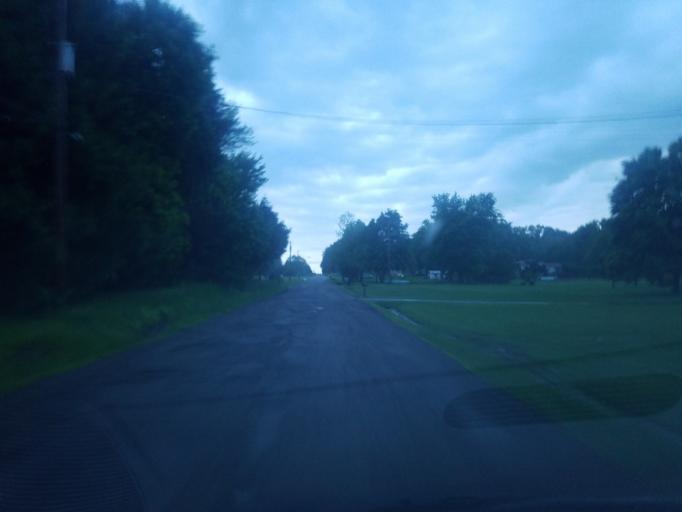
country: US
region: Ohio
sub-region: Mahoning County
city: Canfield
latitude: 40.9728
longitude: -80.7942
